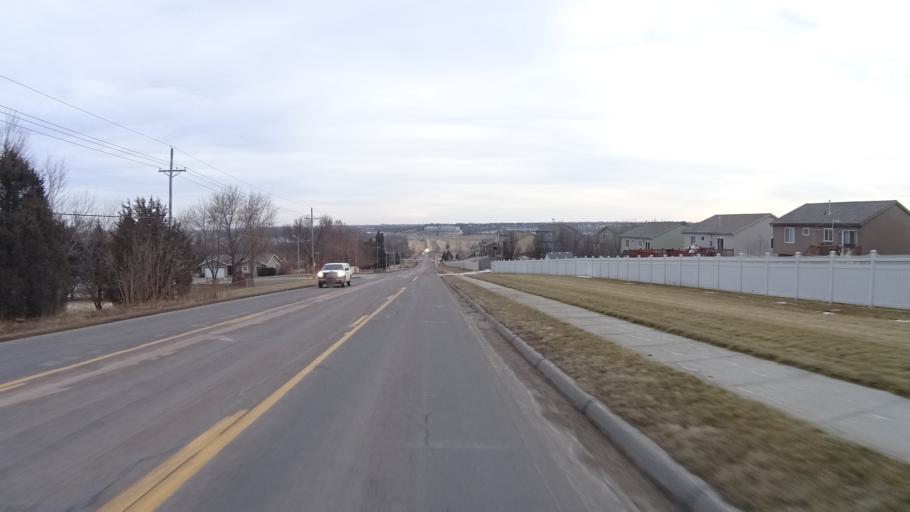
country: US
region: Nebraska
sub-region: Sarpy County
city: Offutt Air Force Base
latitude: 41.1534
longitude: -95.9477
